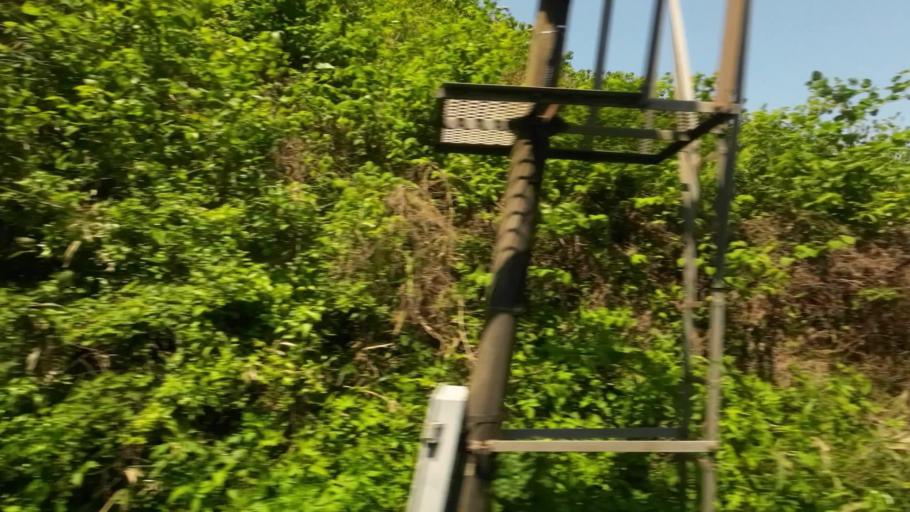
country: JP
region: Ehime
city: Hojo
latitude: 33.9977
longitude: 132.7750
